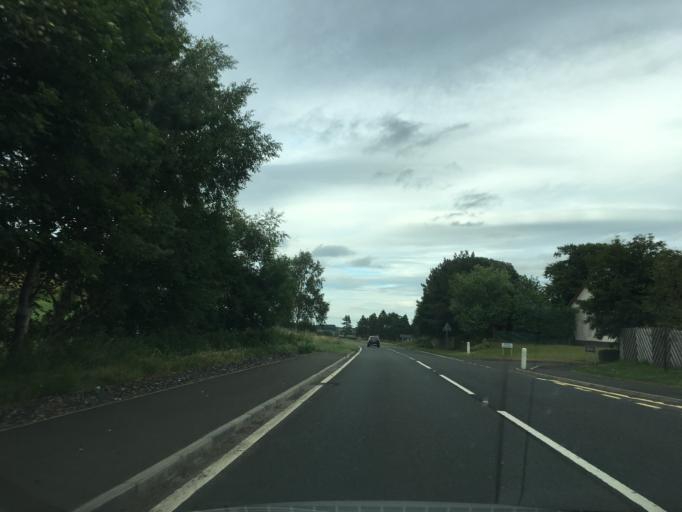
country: GB
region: Scotland
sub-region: The Scottish Borders
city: West Linton
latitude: 55.7161
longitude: -3.4138
